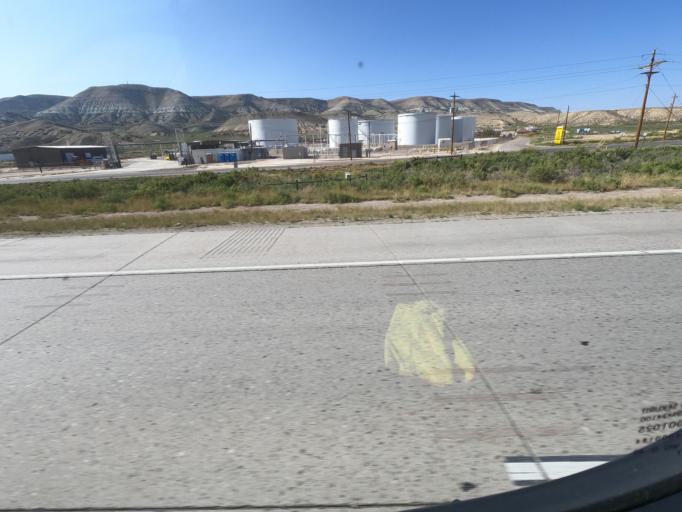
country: US
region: Wyoming
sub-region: Sweetwater County
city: North Rock Springs
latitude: 41.5658
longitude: -109.2915
